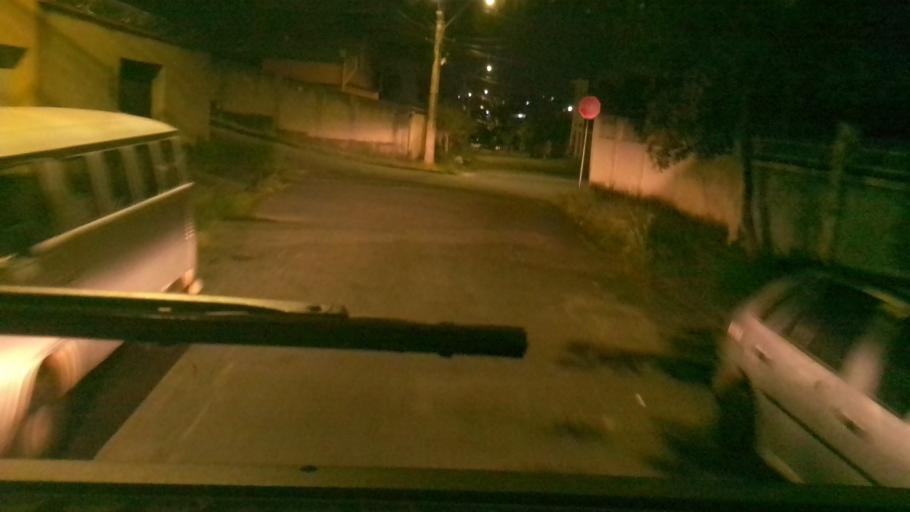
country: BR
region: Minas Gerais
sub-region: Belo Horizonte
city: Belo Horizonte
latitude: -19.8665
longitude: -43.9136
